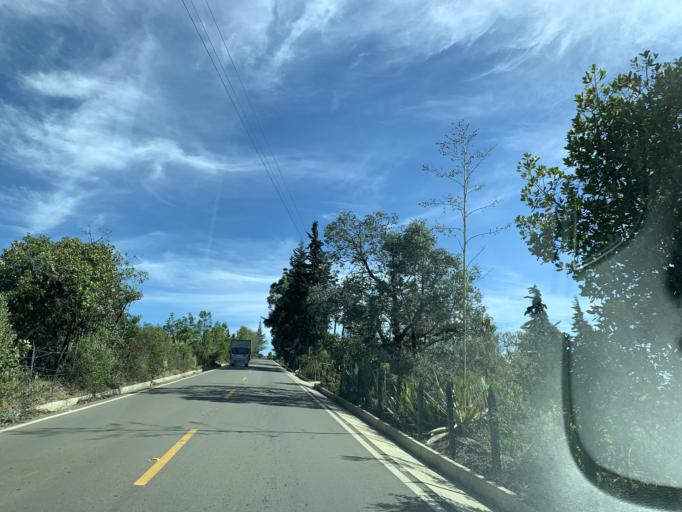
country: CO
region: Boyaca
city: Santa Sofia
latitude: 5.7000
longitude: -73.5907
